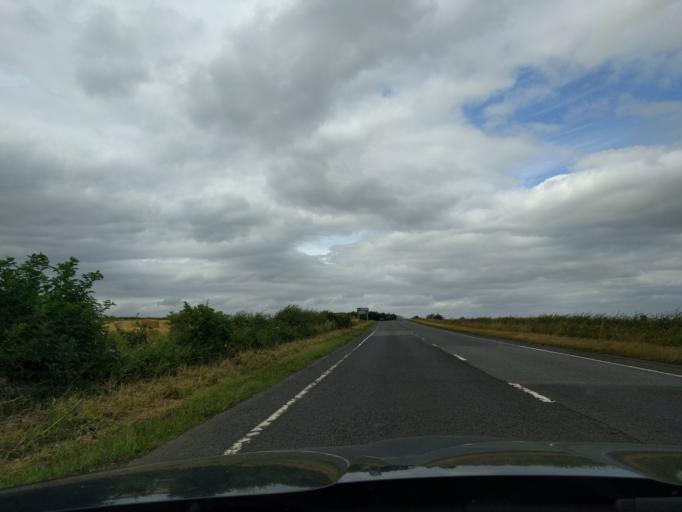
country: GB
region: England
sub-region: Northumberland
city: Ellingham
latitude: 55.5246
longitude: -1.7535
